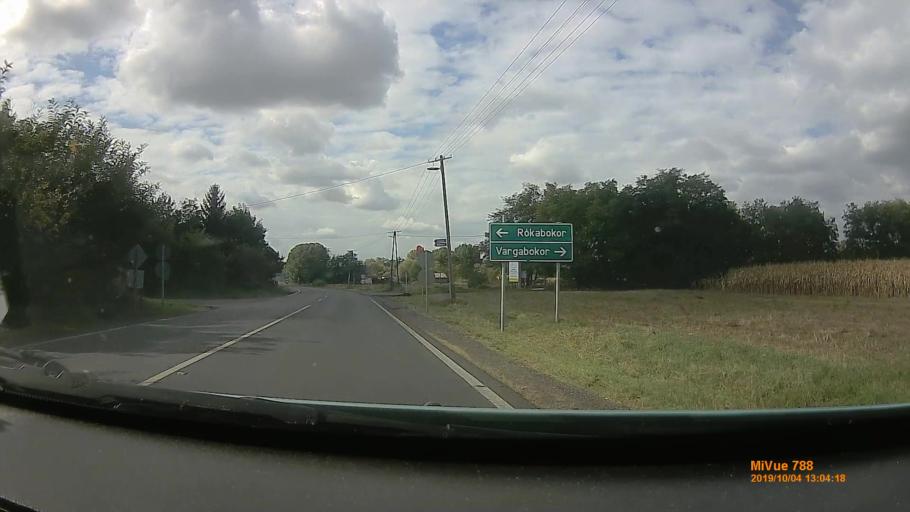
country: HU
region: Szabolcs-Szatmar-Bereg
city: Nyirtelek
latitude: 47.9587
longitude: 21.6296
